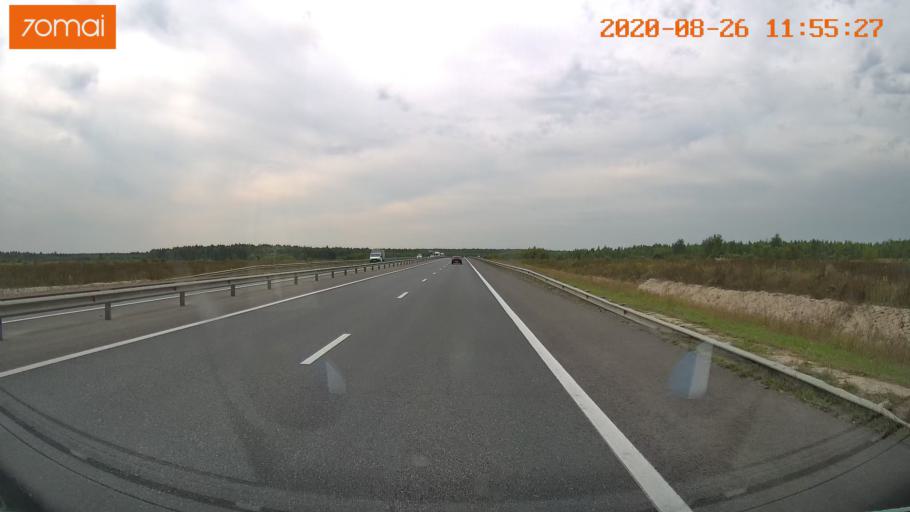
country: RU
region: Rjazan
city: Kiritsy
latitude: 54.2730
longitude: 40.3955
